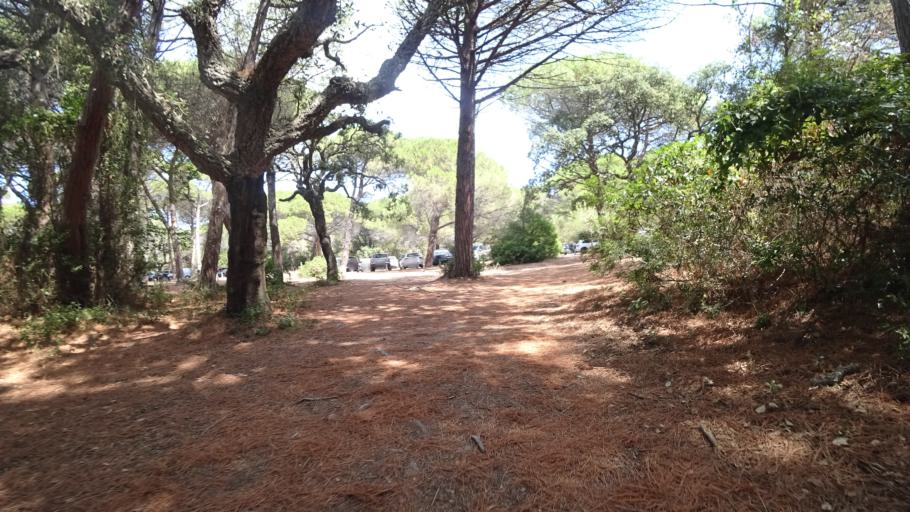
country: FR
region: Corsica
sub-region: Departement de la Corse-du-Sud
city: Porto-Vecchio
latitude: 41.5606
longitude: 9.3367
